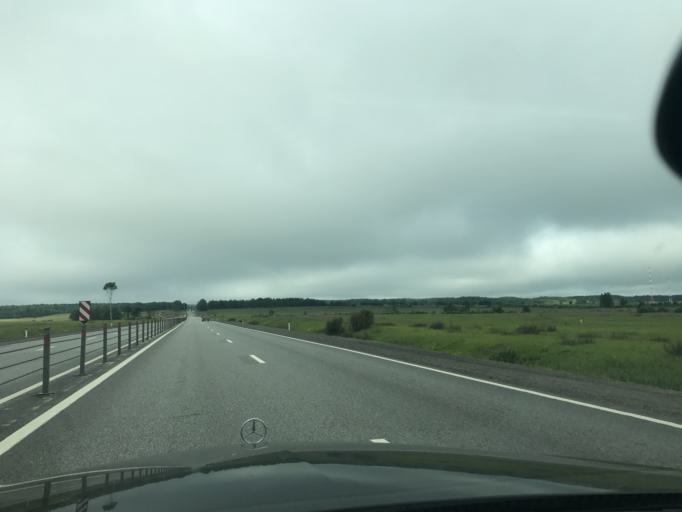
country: RU
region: Smolensk
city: Vyaz'ma
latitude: 55.3400
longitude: 34.5999
